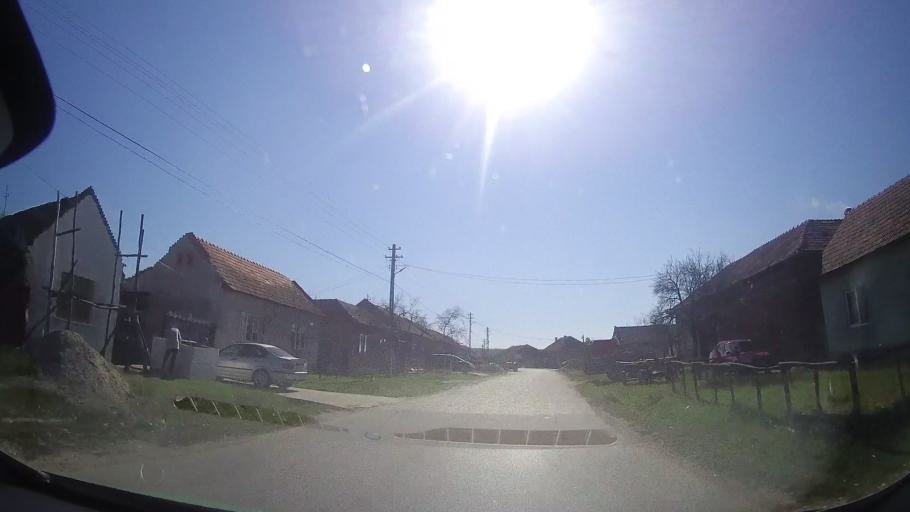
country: RO
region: Timis
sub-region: Comuna Bethausen
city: Bethausen
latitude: 45.8664
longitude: 21.9675
